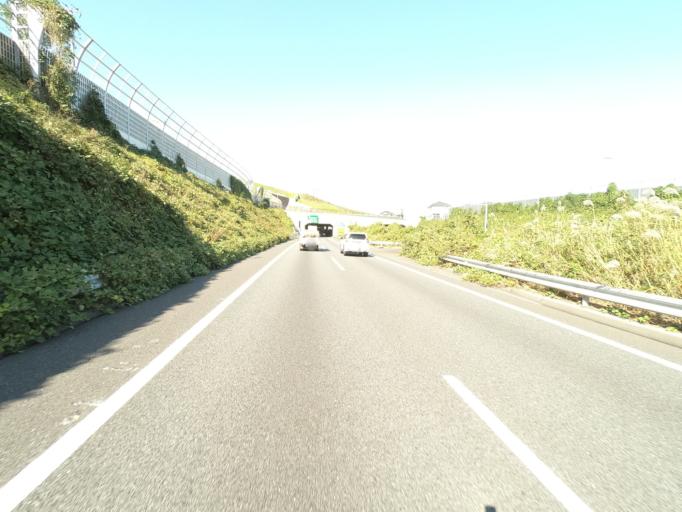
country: JP
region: Kanagawa
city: Zama
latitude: 35.5095
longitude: 139.3613
